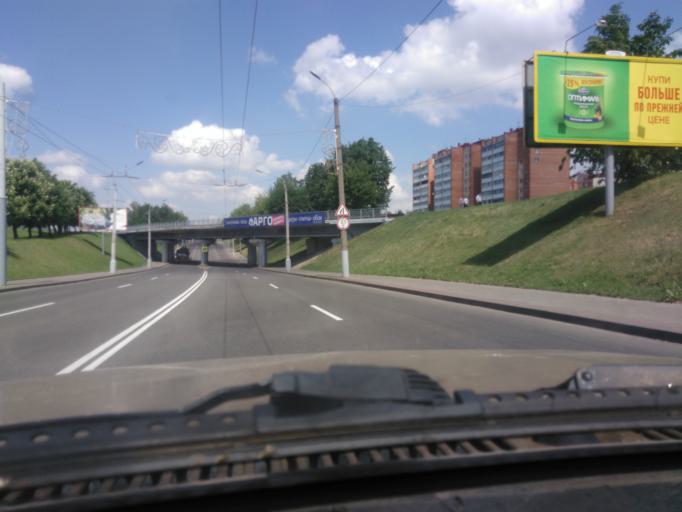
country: BY
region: Mogilev
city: Mahilyow
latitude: 53.9215
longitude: 30.3428
